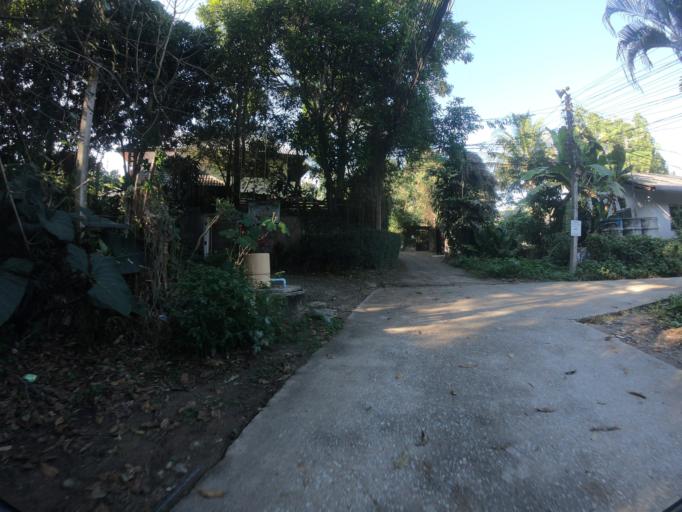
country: TH
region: Chiang Mai
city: Chiang Mai
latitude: 18.7722
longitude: 98.9402
